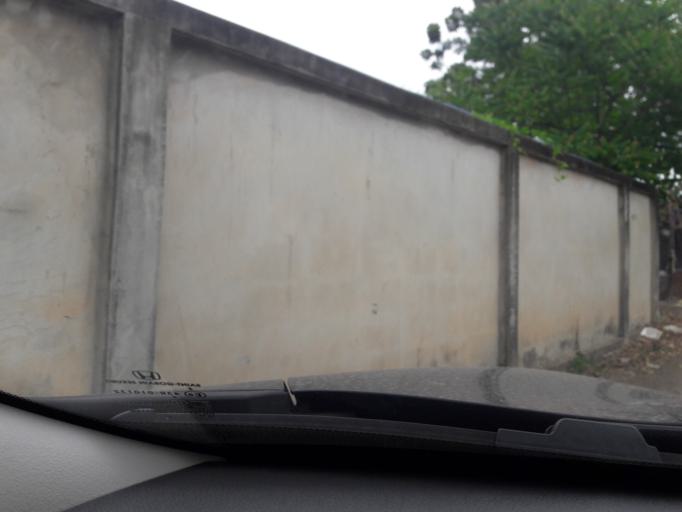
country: TH
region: Ratchaburi
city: Bang Phae
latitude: 13.6009
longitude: 99.9040
